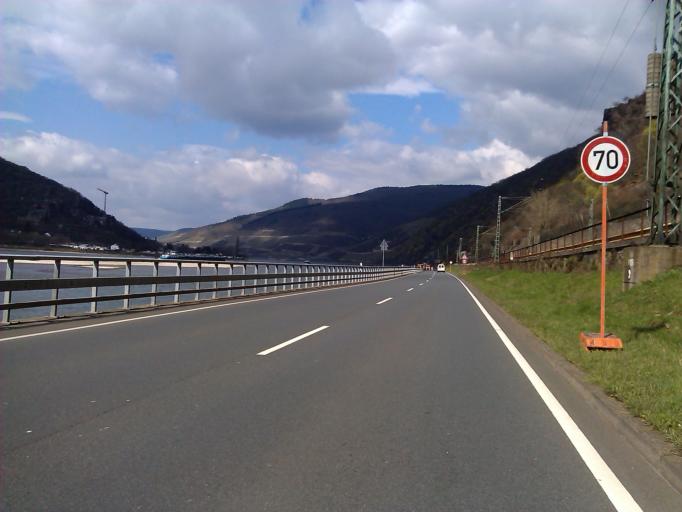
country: DE
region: Rheinland-Pfalz
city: Trechtingshausen
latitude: 49.9987
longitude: 7.8635
